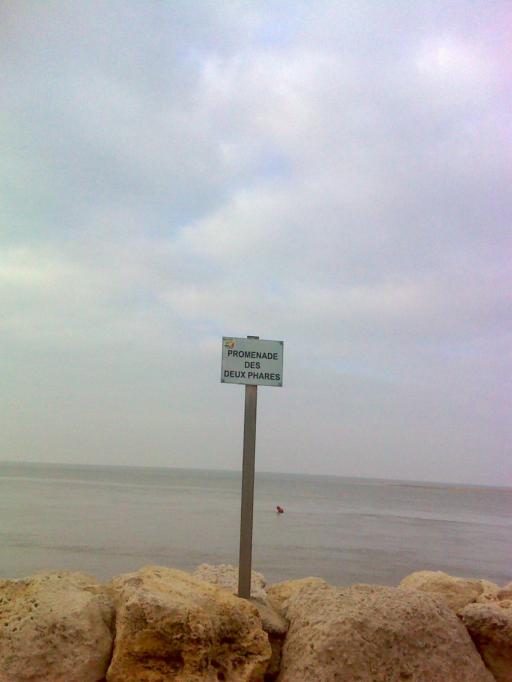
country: FR
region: Poitou-Charentes
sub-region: Departement de la Charente-Maritime
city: Les Mathes
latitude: 45.6786
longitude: -1.1734
